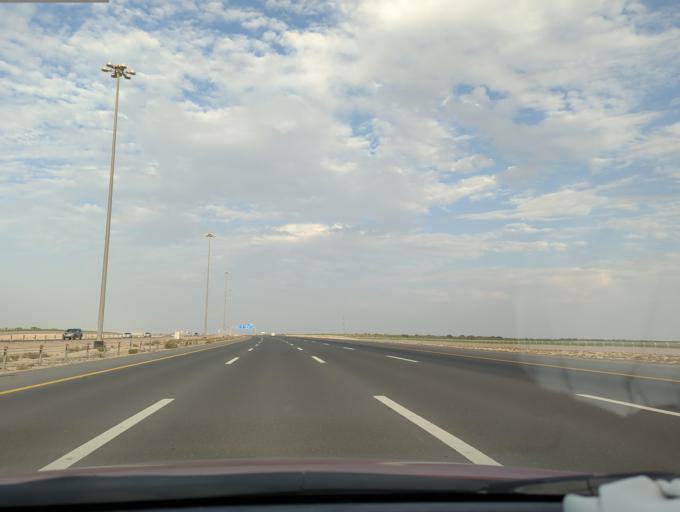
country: AE
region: Dubai
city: Dubai
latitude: 24.7529
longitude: 54.9294
